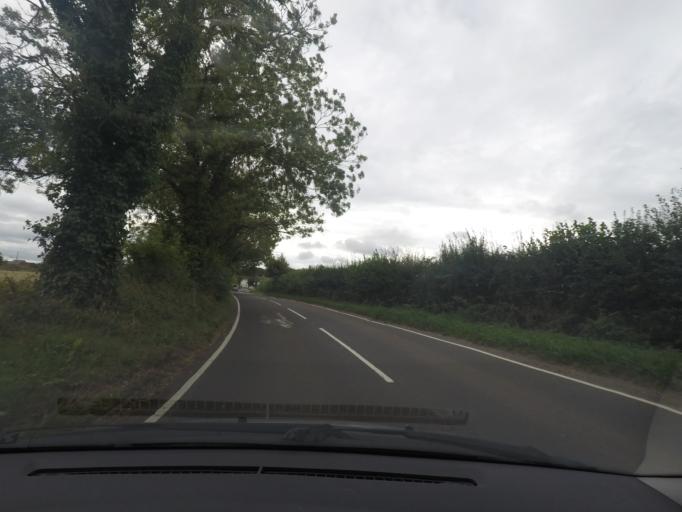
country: GB
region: England
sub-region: Wiltshire
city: Fyfield
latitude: 51.3912
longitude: -1.7552
